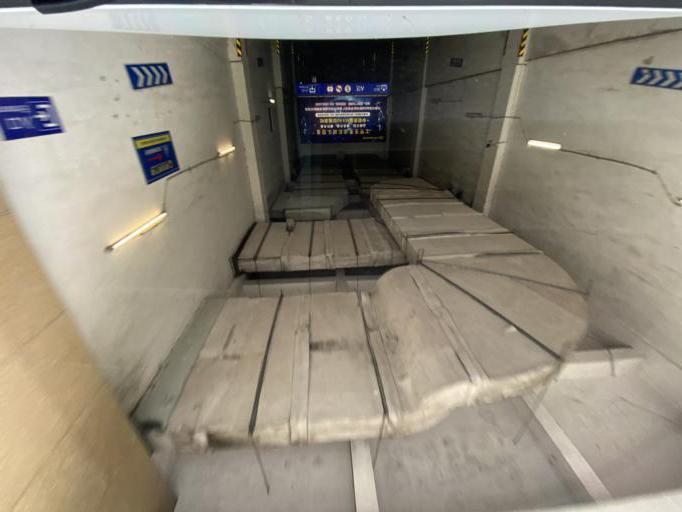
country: CN
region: Hainan
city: Yelin
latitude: 18.5137
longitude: 110.0295
